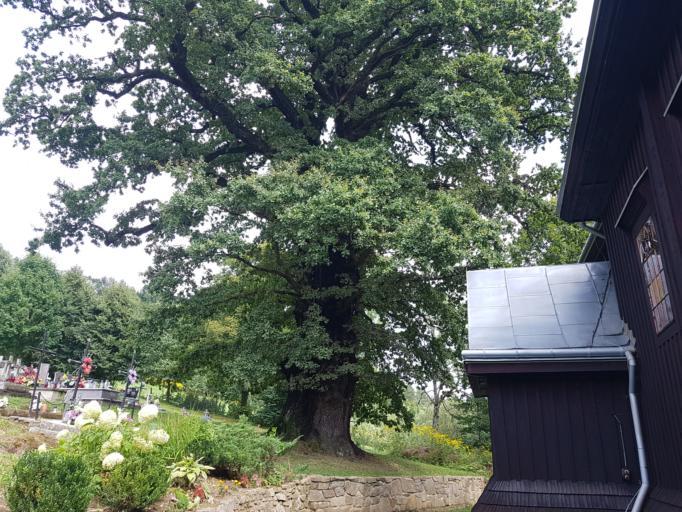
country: PL
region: Subcarpathian Voivodeship
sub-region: Powiat leski
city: Polanczyk
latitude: 49.3280
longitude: 22.3763
